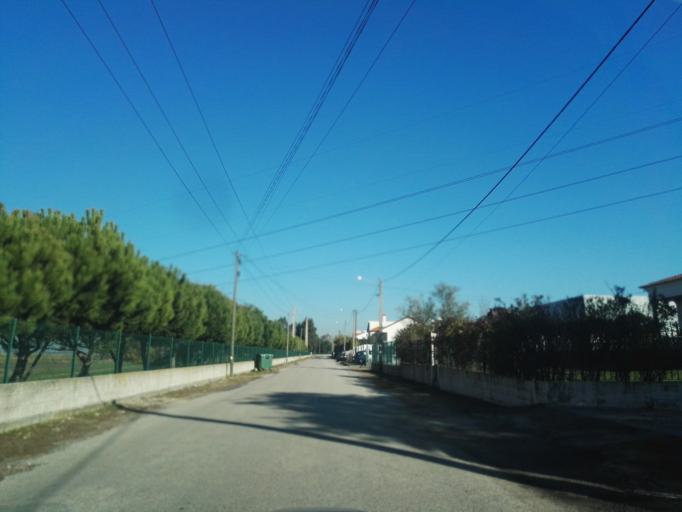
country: PT
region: Santarem
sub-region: Benavente
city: Samora Correia
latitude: 38.9315
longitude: -8.8822
